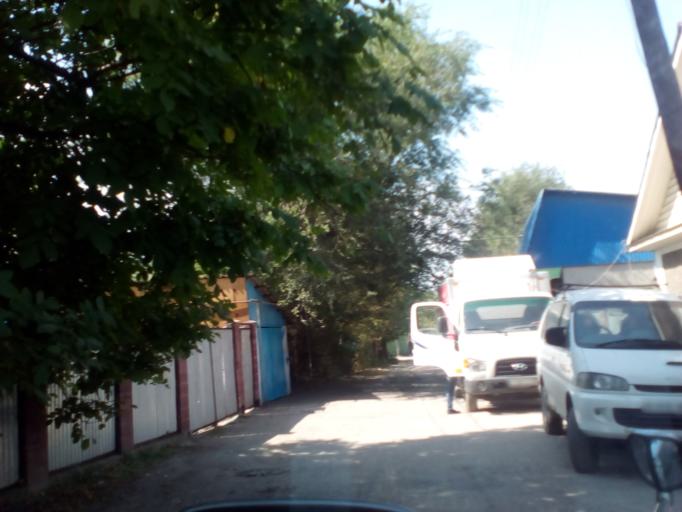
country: KZ
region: Almaty Oblysy
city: Burunday
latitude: 43.1600
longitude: 76.4045
